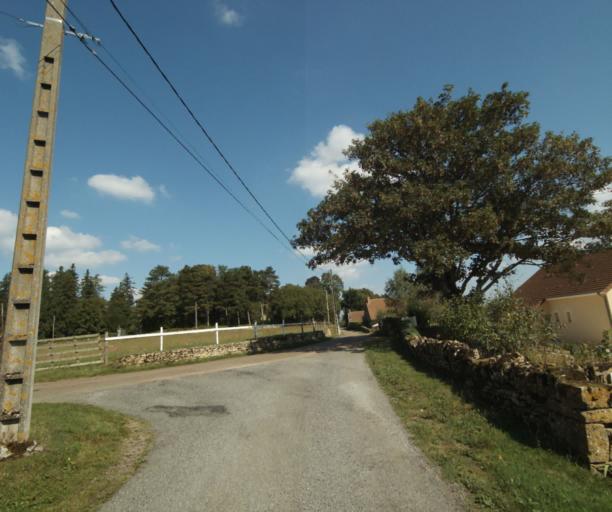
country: FR
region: Bourgogne
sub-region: Departement de Saone-et-Loire
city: Charolles
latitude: 46.3785
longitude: 4.2357
